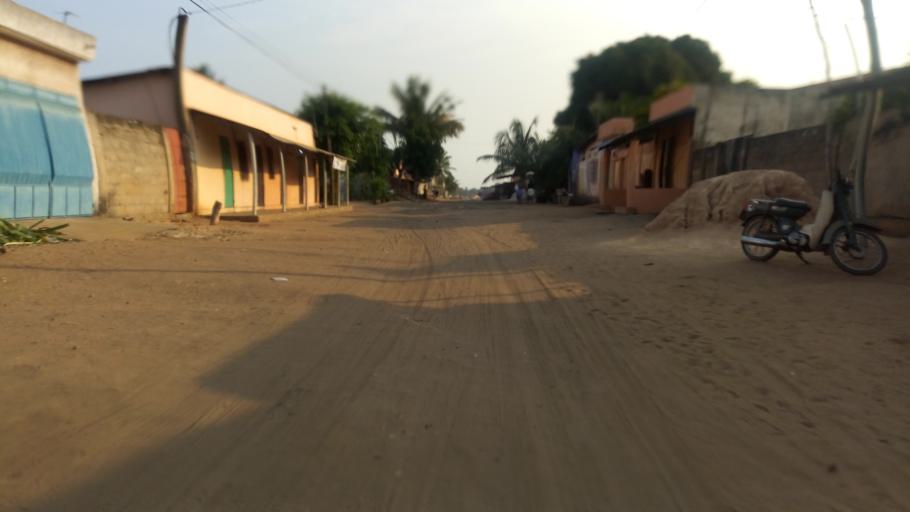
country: TG
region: Maritime
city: Lome
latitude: 6.1915
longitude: 1.1779
